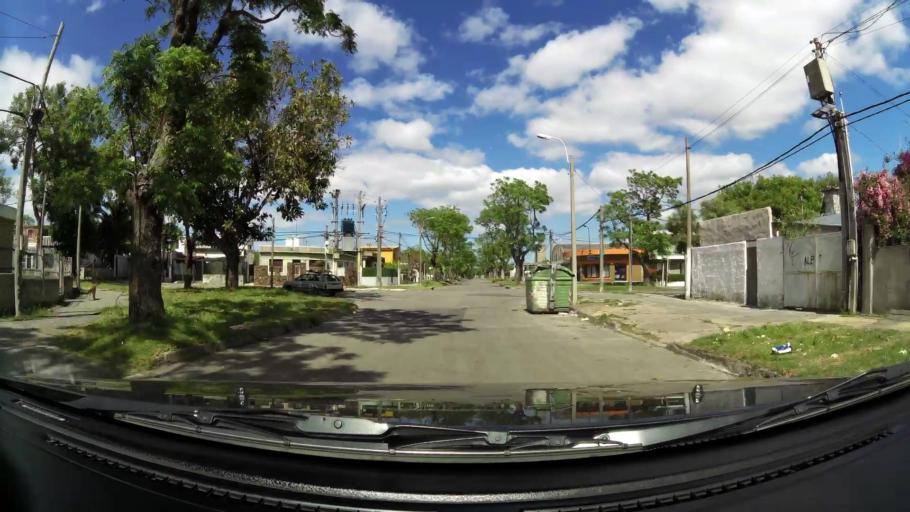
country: UY
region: Canelones
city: Paso de Carrasco
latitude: -34.8703
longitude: -56.1204
